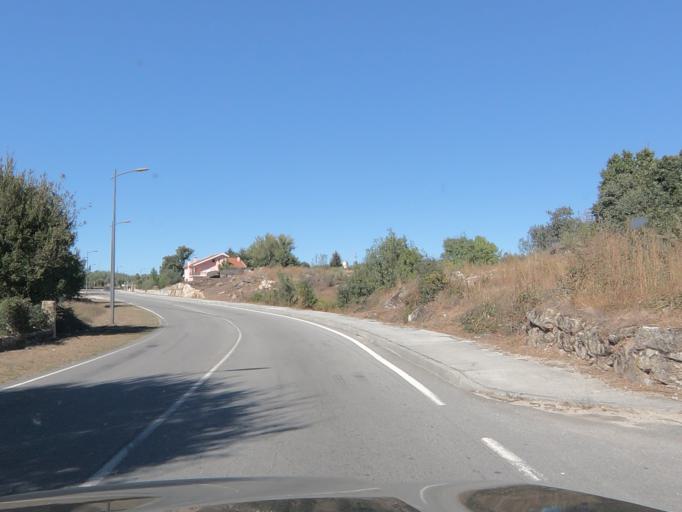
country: PT
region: Vila Real
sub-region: Valpacos
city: Valpacos
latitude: 41.5862
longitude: -7.3062
